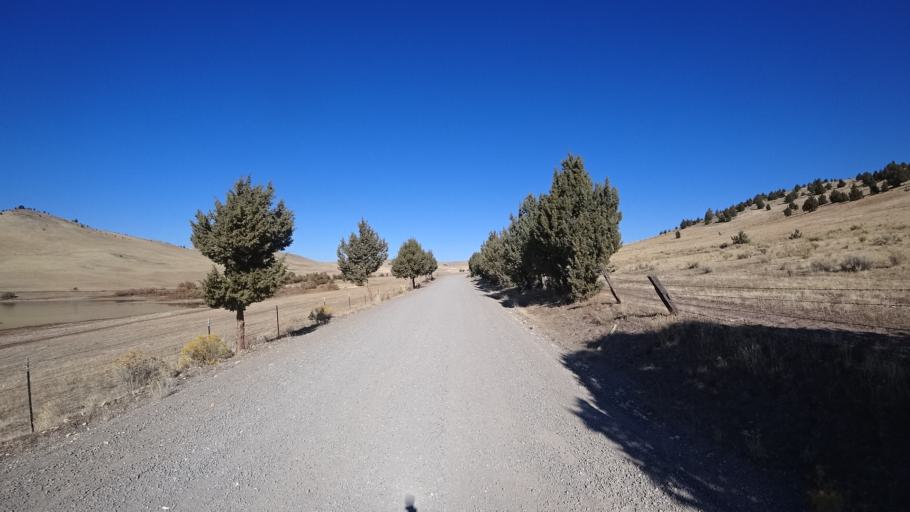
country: US
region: California
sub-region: Siskiyou County
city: Montague
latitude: 41.7313
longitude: -122.3694
